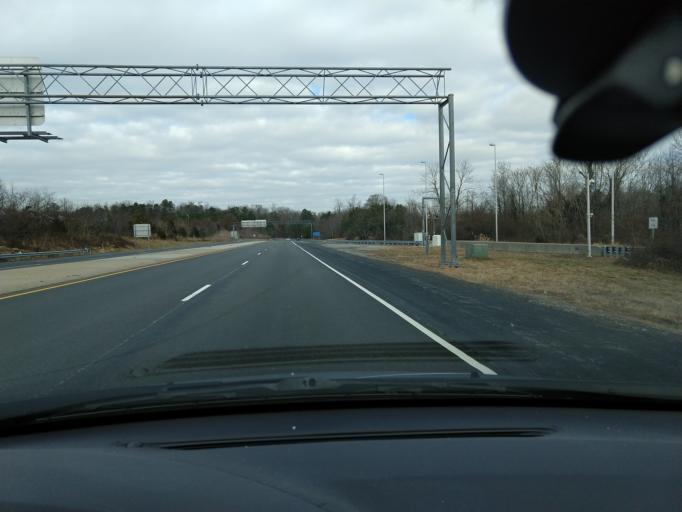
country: US
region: Virginia
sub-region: Chesterfield County
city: Bensley
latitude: 37.4599
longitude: -77.3849
